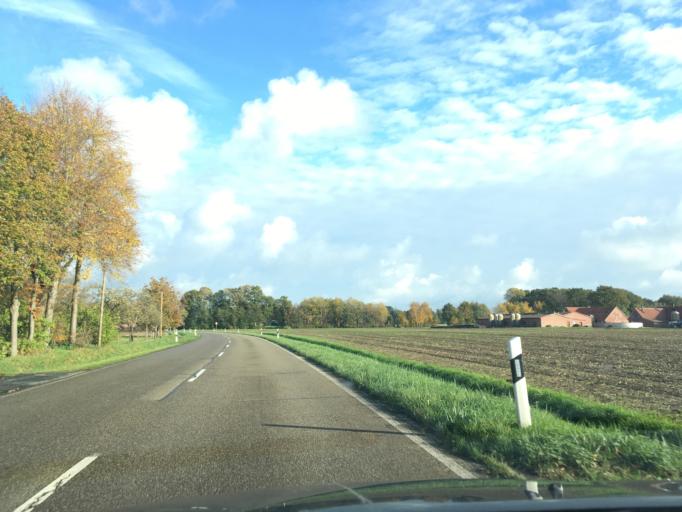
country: DE
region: North Rhine-Westphalia
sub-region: Regierungsbezirk Munster
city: Vreden
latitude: 52.0942
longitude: 6.8390
